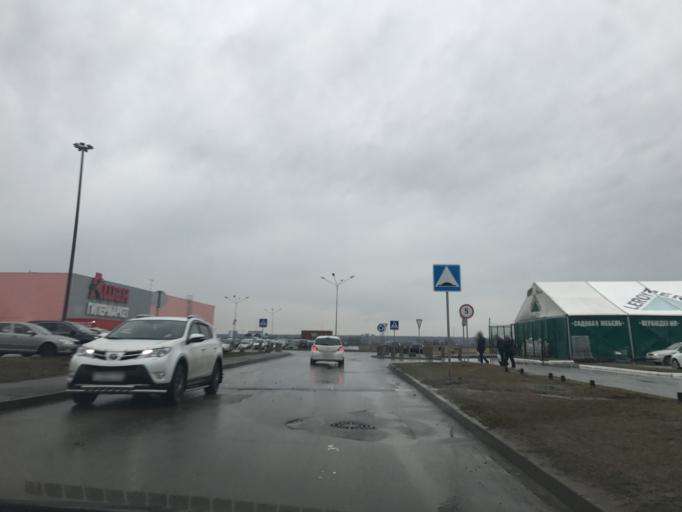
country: RU
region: Rostov
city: Severnyy
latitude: 47.3087
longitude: 39.7248
